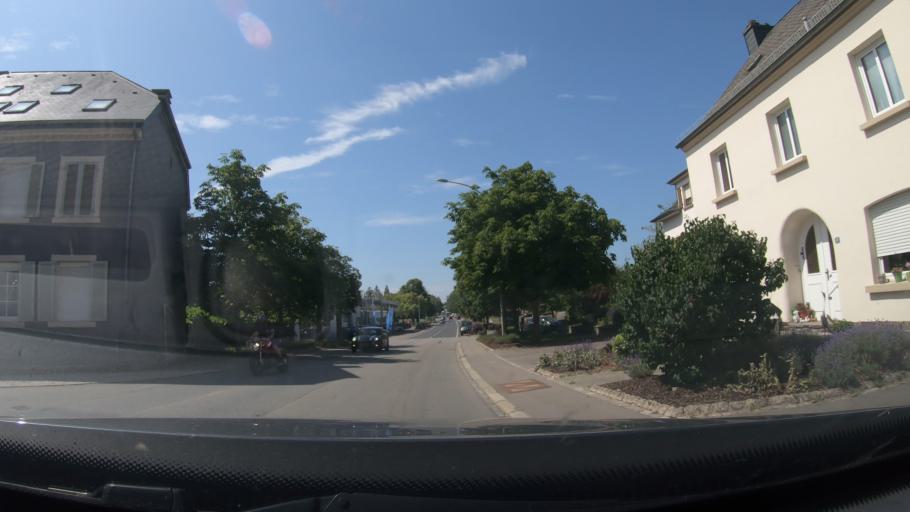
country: LU
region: Diekirch
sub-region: Canton de Clervaux
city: Hosingen
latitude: 50.0148
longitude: 6.0917
